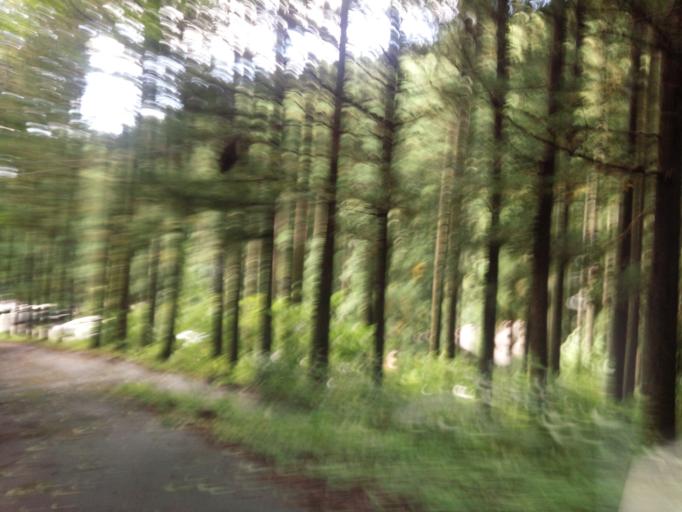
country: JP
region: Gunma
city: Nakanojomachi
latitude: 36.6977
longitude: 138.7737
